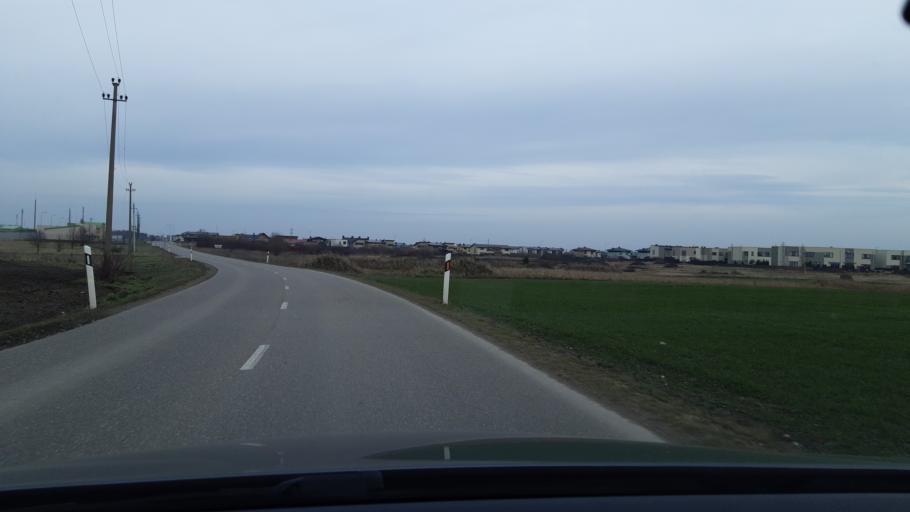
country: LT
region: Kauno apskritis
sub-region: Kaunas
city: Sargenai
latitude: 54.9496
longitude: 23.8428
